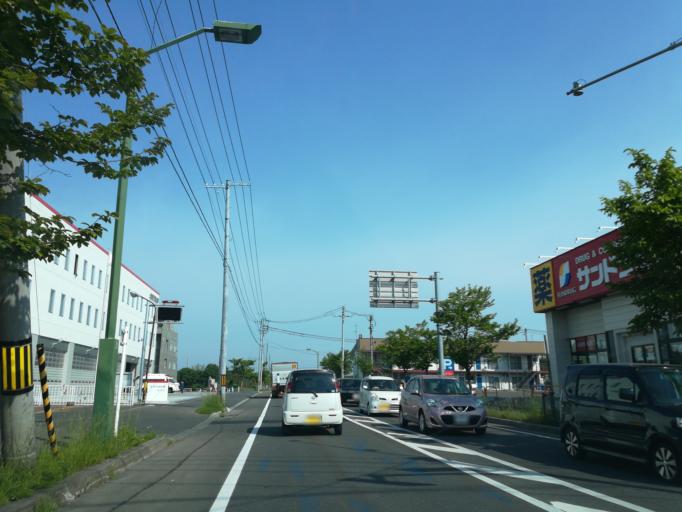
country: JP
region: Hokkaido
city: Iwamizawa
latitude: 43.2035
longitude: 141.7815
